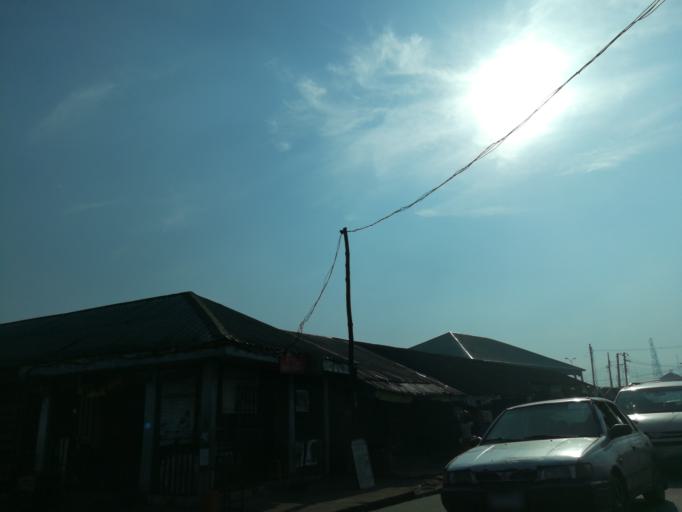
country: NG
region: Rivers
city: Port Harcourt
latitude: 4.8124
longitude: 7.0184
